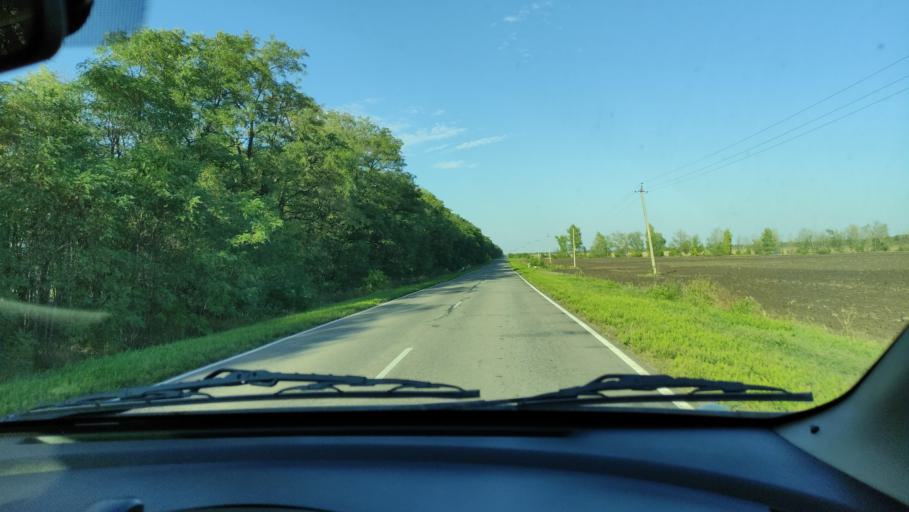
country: RU
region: Voronezj
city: Verkhniy Mamon
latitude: 50.1288
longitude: 40.3204
